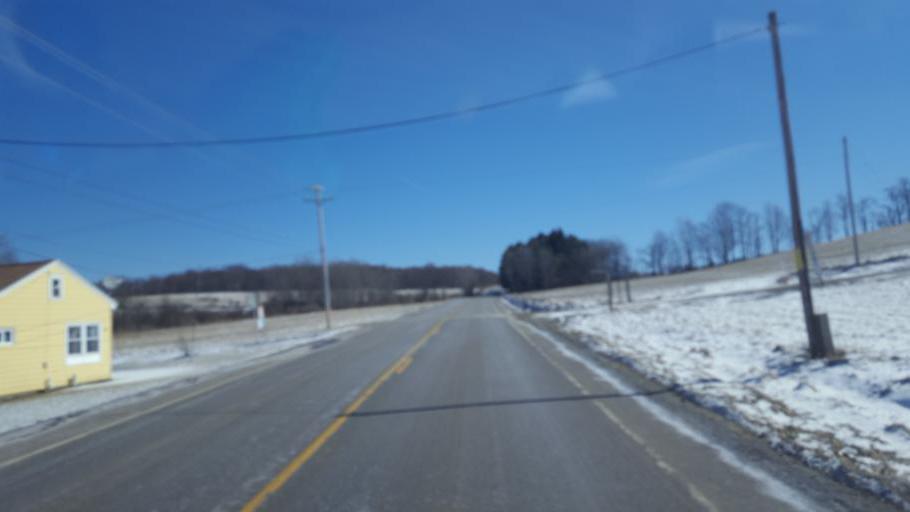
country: US
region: New York
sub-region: Allegany County
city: Andover
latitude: 42.0669
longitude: -77.8118
